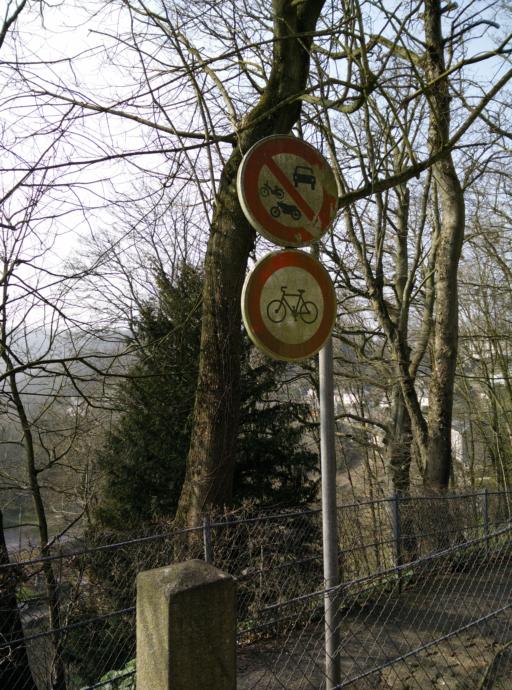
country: FR
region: Lower Normandy
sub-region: Departement du Calvados
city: Vire
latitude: 48.8363
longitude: -0.8926
